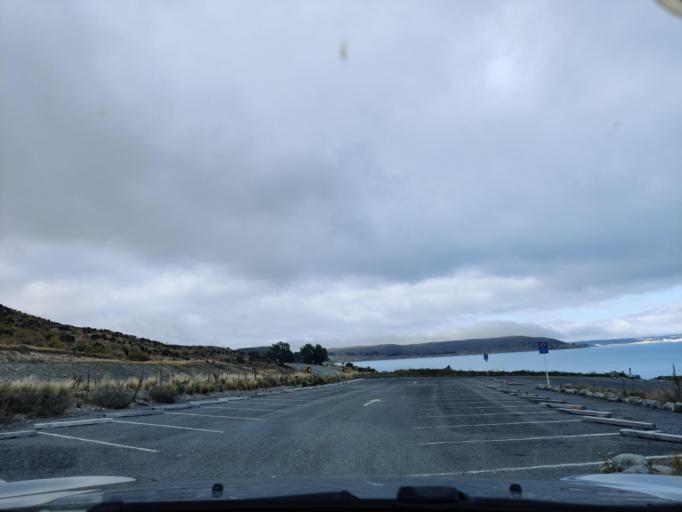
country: NZ
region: Canterbury
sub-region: Timaru District
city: Pleasant Point
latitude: -44.1684
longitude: 170.2100
